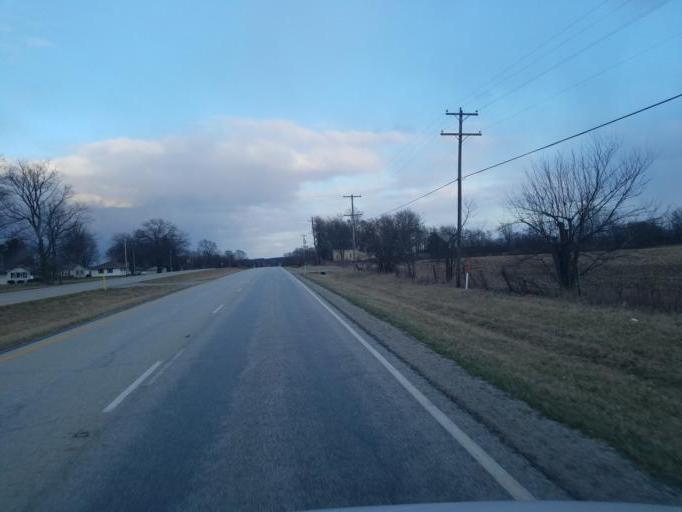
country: US
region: Indiana
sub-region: Henry County
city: Knightstown
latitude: 39.7935
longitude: -85.5543
